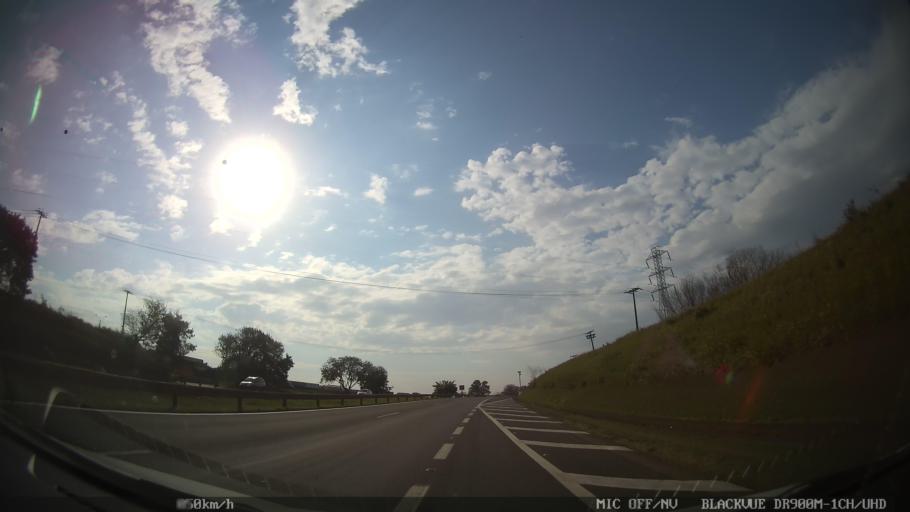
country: BR
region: Sao Paulo
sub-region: Paulinia
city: Paulinia
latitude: -22.7925
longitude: -47.1352
